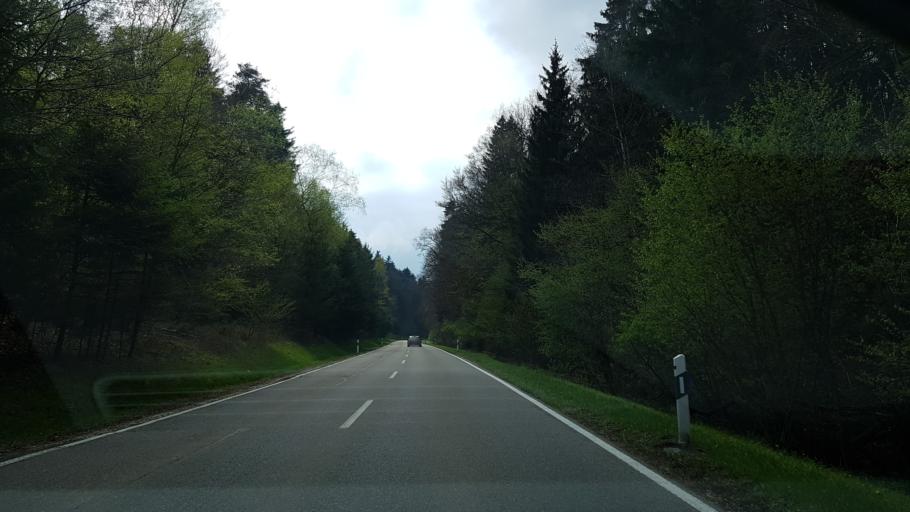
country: DE
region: Baden-Wuerttemberg
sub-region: Tuebingen Region
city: Dietenheim
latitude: 48.2034
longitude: 10.0516
